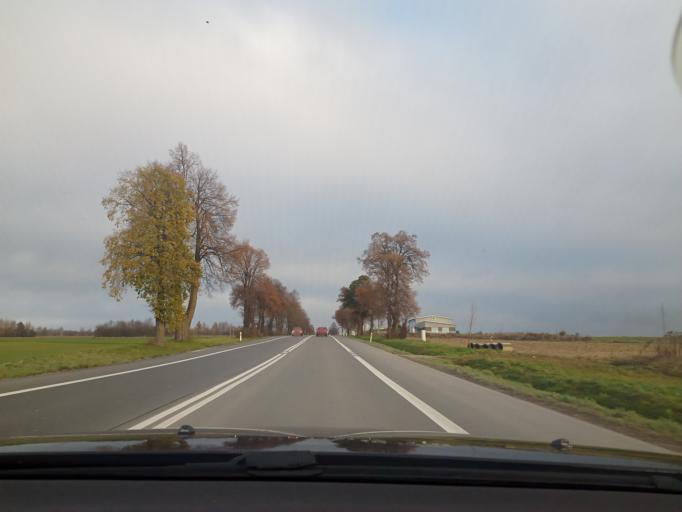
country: PL
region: Lesser Poland Voivodeship
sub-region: Powiat miechowski
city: Miechow
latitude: 50.3252
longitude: 20.0334
